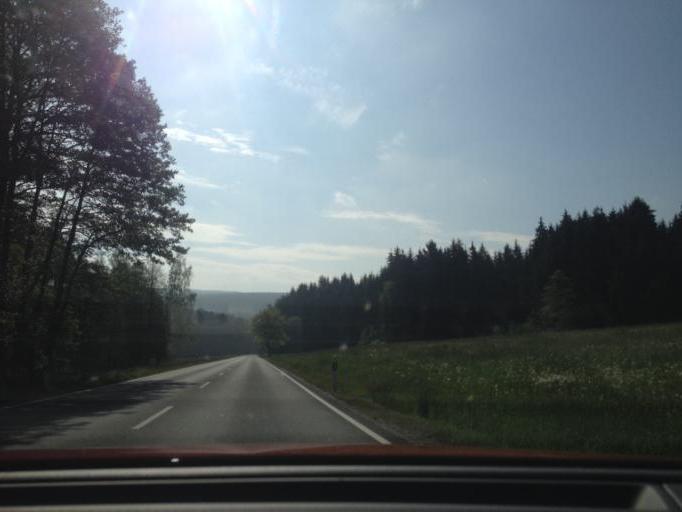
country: DE
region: Bavaria
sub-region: Upper Palatinate
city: Neusorg
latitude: 49.9086
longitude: 11.9571
